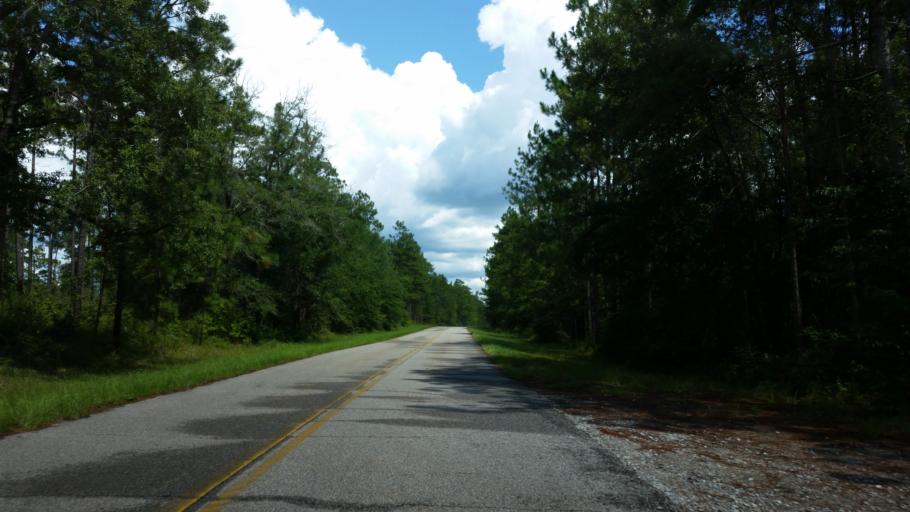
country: US
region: Florida
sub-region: Santa Rosa County
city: East Milton
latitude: 30.7418
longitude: -86.8258
